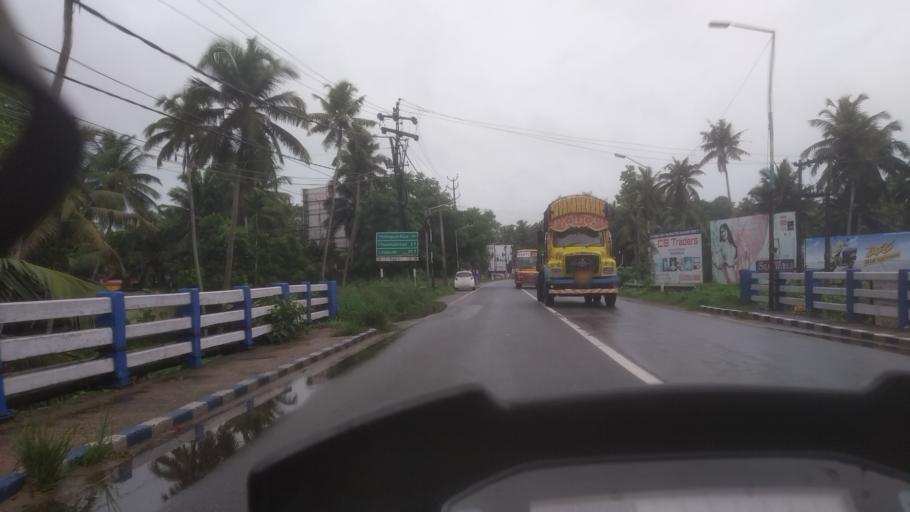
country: IN
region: Kerala
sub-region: Alappuzha
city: Kayankulam
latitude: 9.1530
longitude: 76.5115
